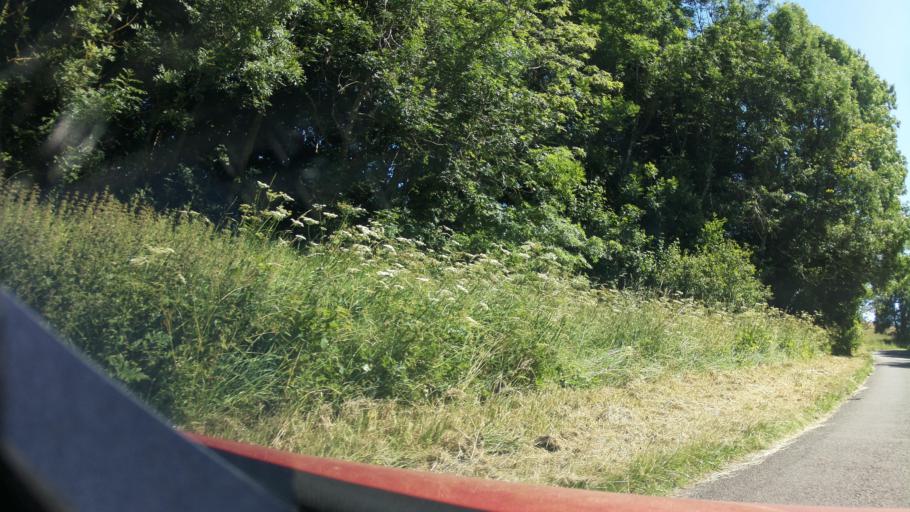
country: GB
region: England
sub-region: Derbyshire
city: Buxton
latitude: 53.2872
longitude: -1.8619
